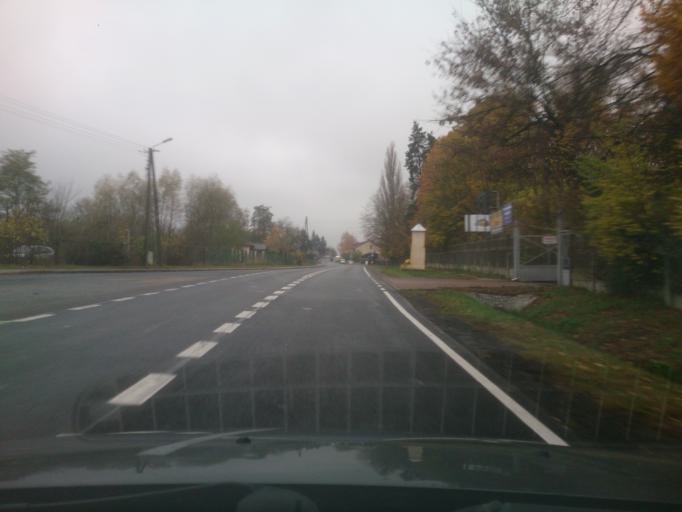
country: PL
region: Greater Poland Voivodeship
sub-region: Powiat kolski
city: Kolo
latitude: 52.2642
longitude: 18.6823
